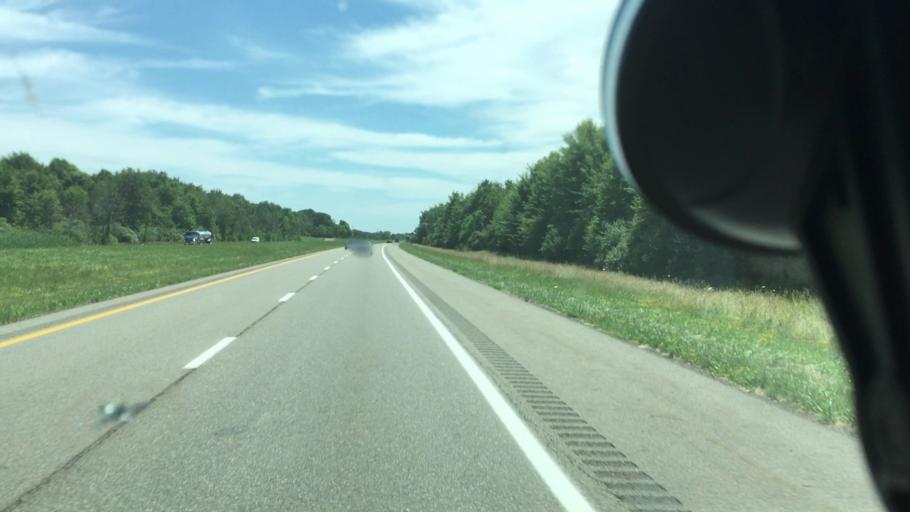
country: US
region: Ohio
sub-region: Columbiana County
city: Columbiana
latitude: 40.9587
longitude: -80.7196
